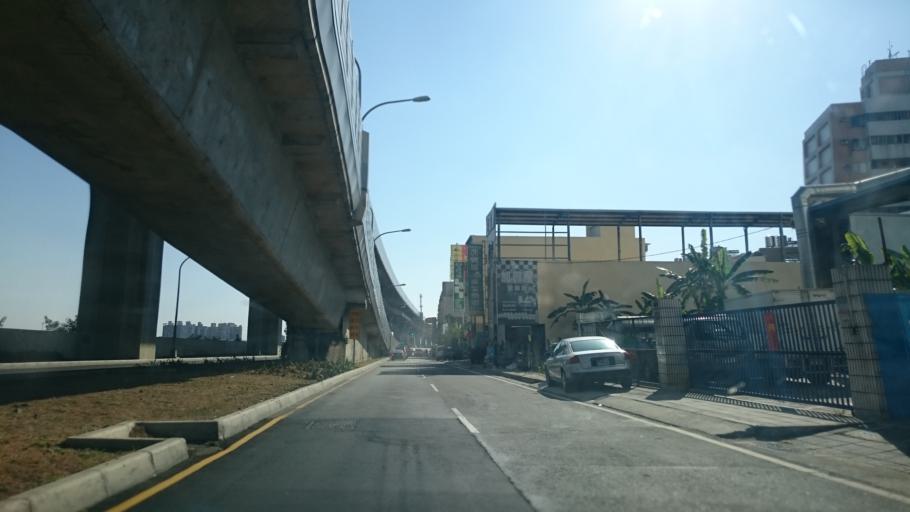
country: TW
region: Taiwan
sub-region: Taichung City
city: Taichung
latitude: 24.1038
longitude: 120.6929
